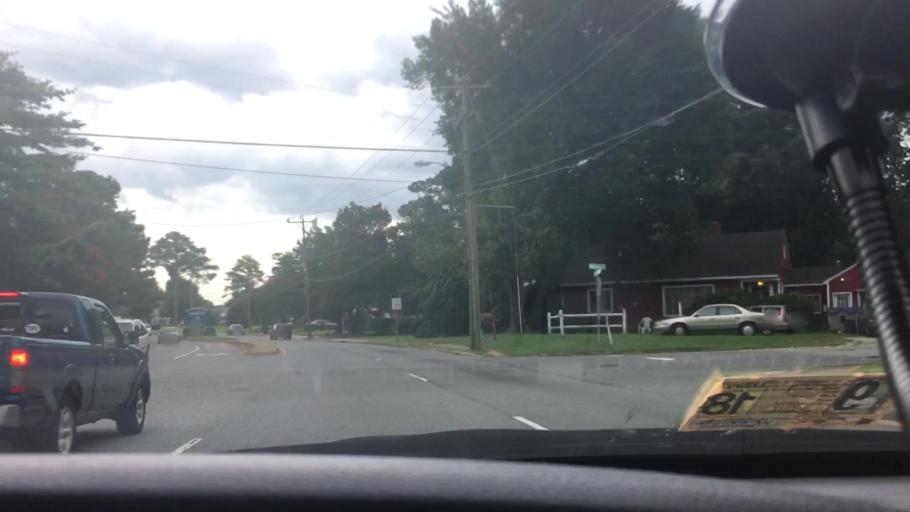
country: US
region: Virginia
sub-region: City of Portsmouth
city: Portsmouth Heights
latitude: 36.8226
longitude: -76.3962
